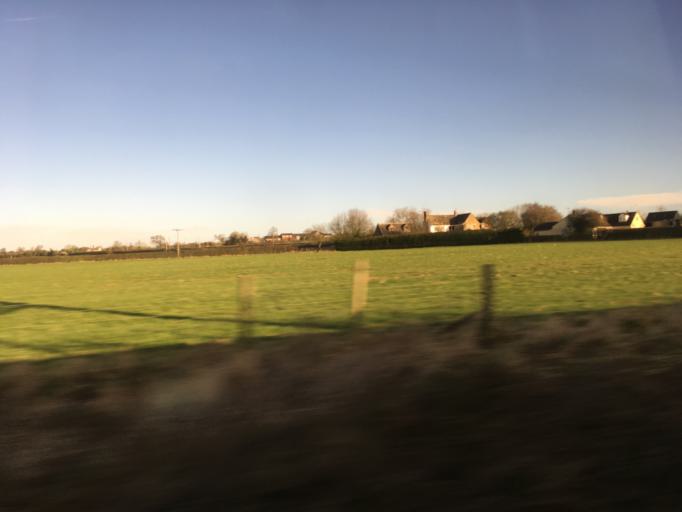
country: GB
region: England
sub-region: Wiltshire
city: Lydiard Tregoze
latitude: 51.5367
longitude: -1.8715
